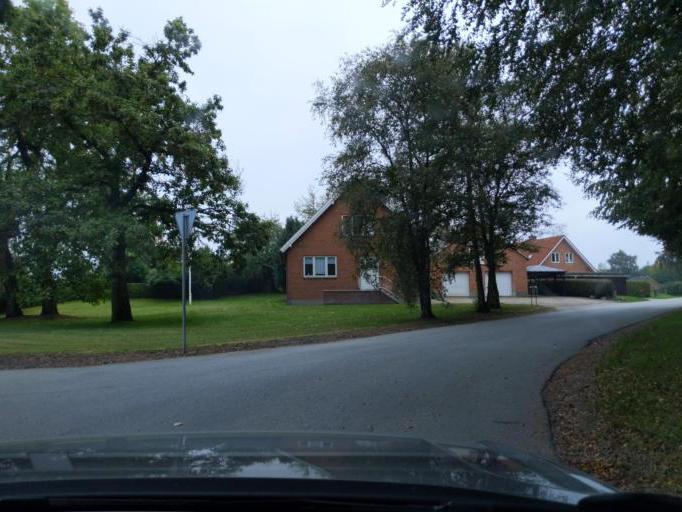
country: DK
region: Central Jutland
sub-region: Viborg Kommune
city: Viborg
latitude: 56.4822
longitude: 9.3039
